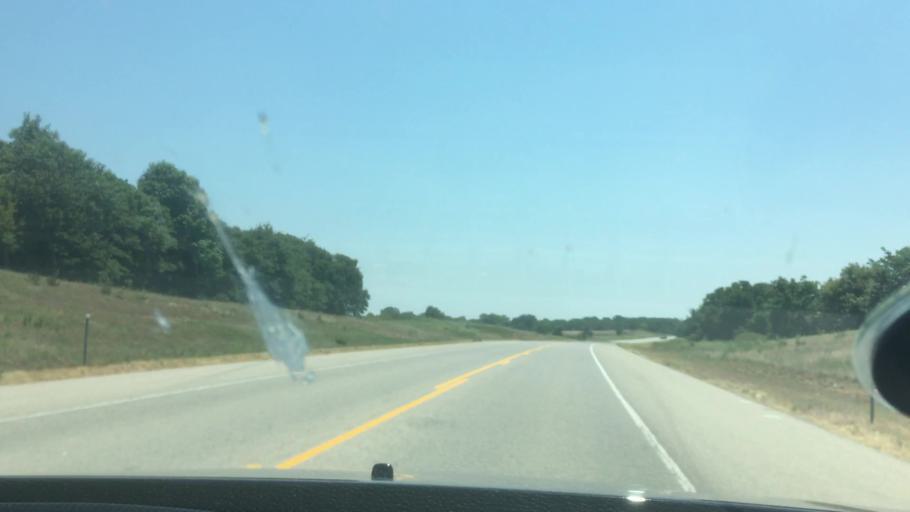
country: US
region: Oklahoma
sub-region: Pontotoc County
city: Ada
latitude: 34.6761
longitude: -96.5752
